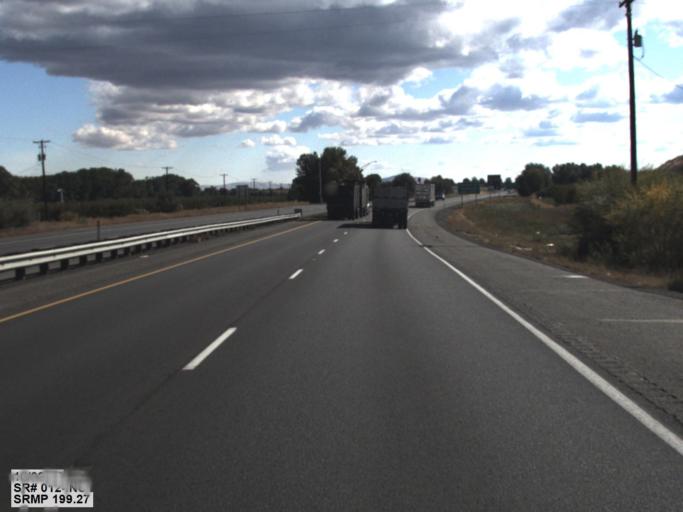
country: US
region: Washington
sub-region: Yakima County
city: West Valley
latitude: 46.6272
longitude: -120.5764
